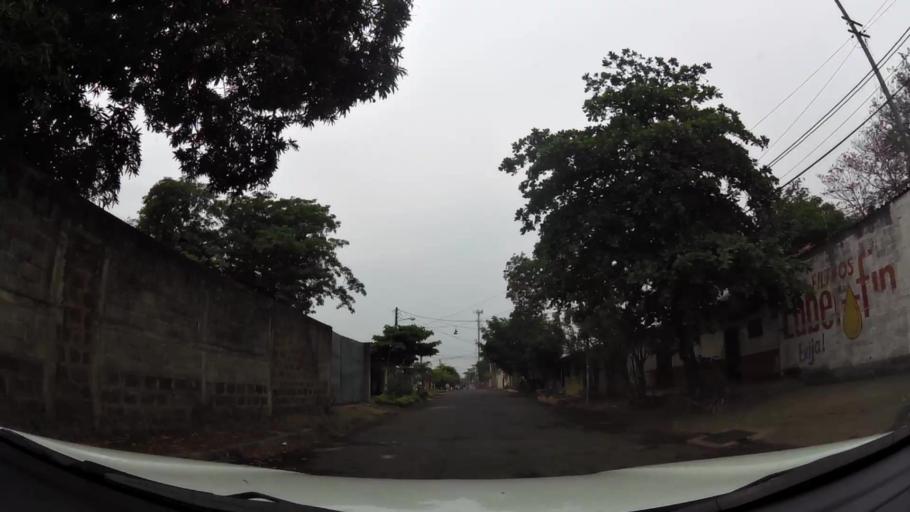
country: NI
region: Leon
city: Leon
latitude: 12.4488
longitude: -86.8718
